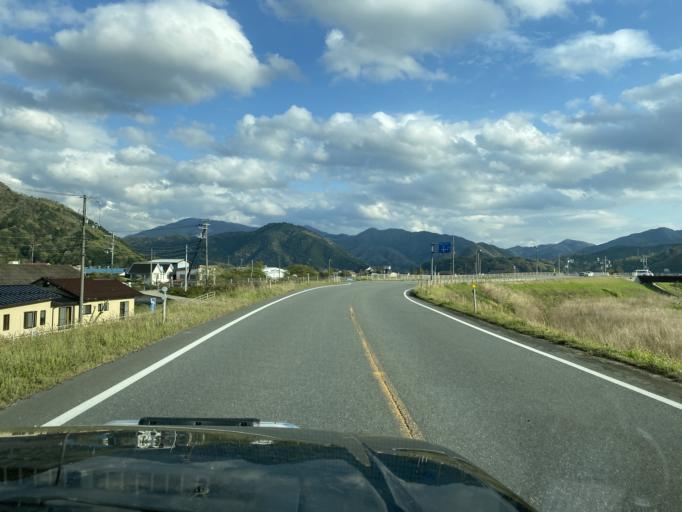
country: JP
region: Hyogo
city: Toyooka
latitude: 35.4822
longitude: 134.8619
